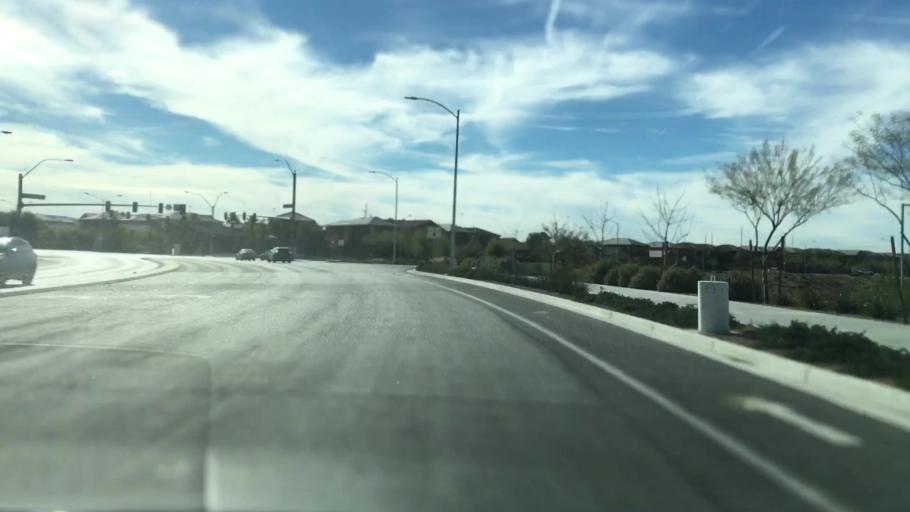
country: US
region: Nevada
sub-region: Clark County
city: Whitney
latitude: 36.0720
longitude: -115.0282
